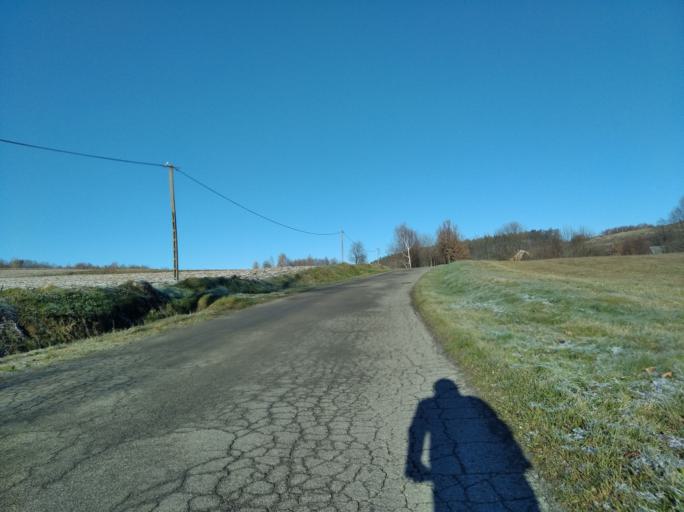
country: PL
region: Subcarpathian Voivodeship
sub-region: Powiat strzyzowski
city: Czudec
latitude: 49.9409
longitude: 21.7878
